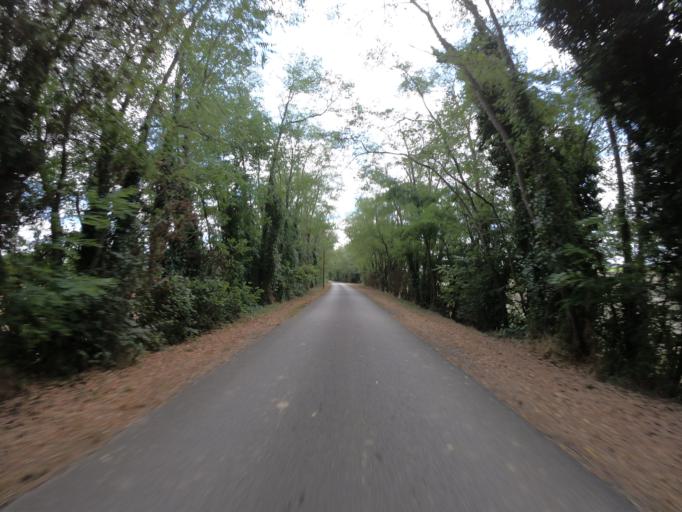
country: FR
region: Midi-Pyrenees
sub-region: Departement de l'Ariege
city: La Tour-du-Crieu
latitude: 43.1002
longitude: 1.7295
